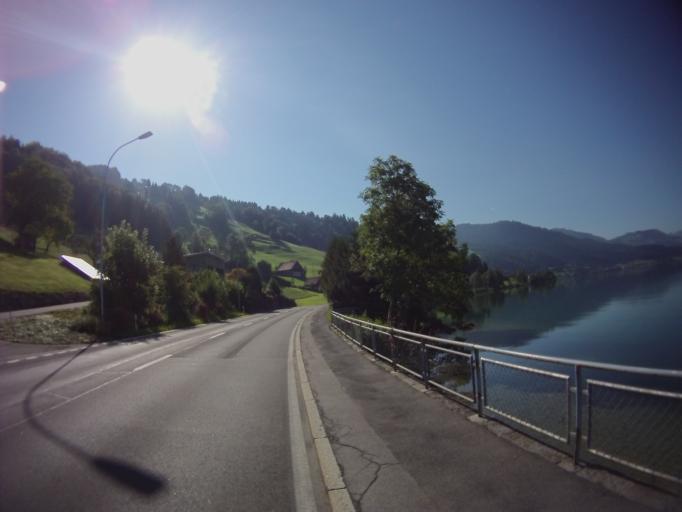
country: CH
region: Schwyz
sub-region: Bezirk Schwyz
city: Sattel
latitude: 47.1268
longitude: 8.6325
